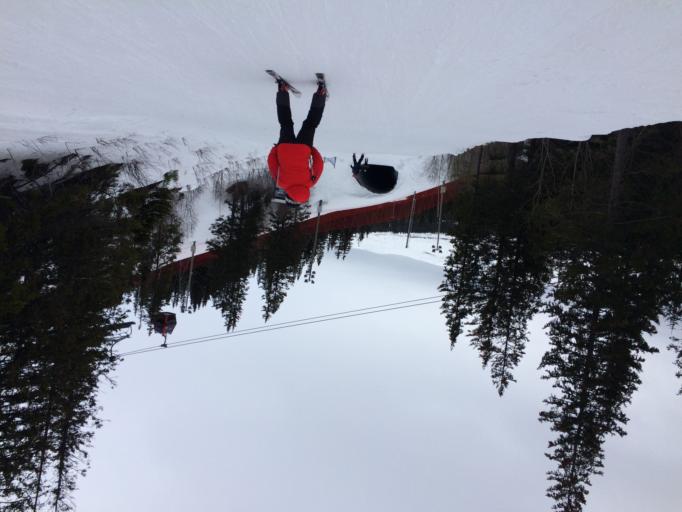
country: SE
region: Jaemtland
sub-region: Are Kommun
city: Are
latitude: 63.4113
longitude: 13.0632
